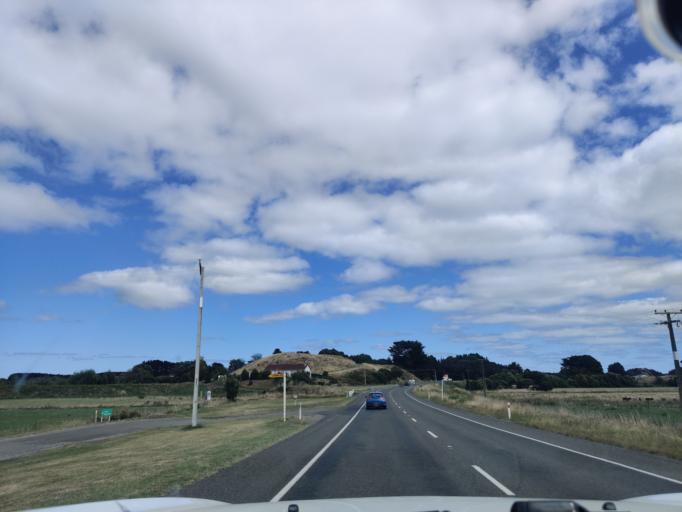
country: NZ
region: Manawatu-Wanganui
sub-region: Horowhenua District
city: Foxton
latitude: -40.4227
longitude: 175.4441
